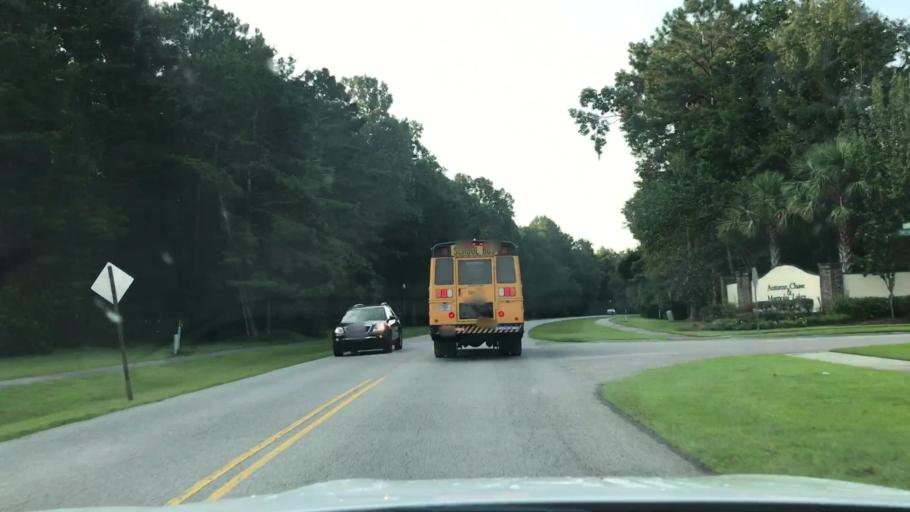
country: US
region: South Carolina
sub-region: Charleston County
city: Shell Point
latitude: 32.8311
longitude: -80.0877
